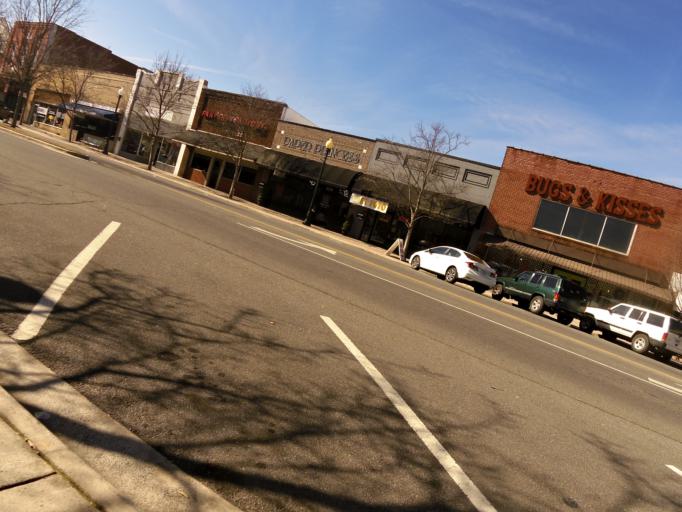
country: US
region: Georgia
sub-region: Whitfield County
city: Dalton
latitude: 34.7739
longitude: -84.9678
